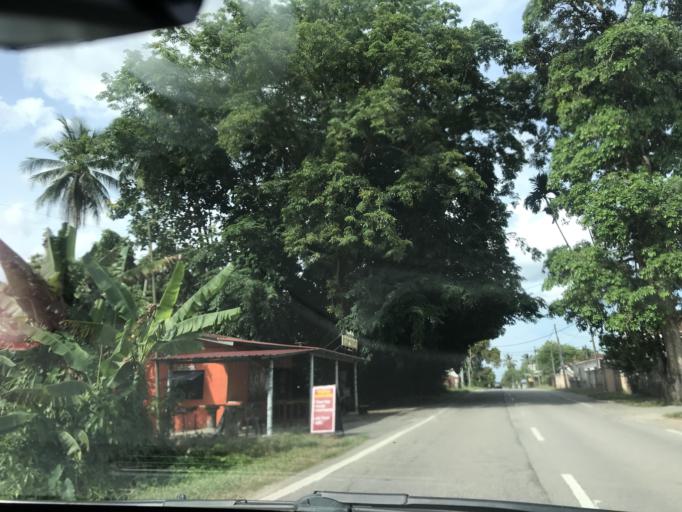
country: MY
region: Kelantan
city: Kampung Lemal
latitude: 6.0334
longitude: 102.1672
